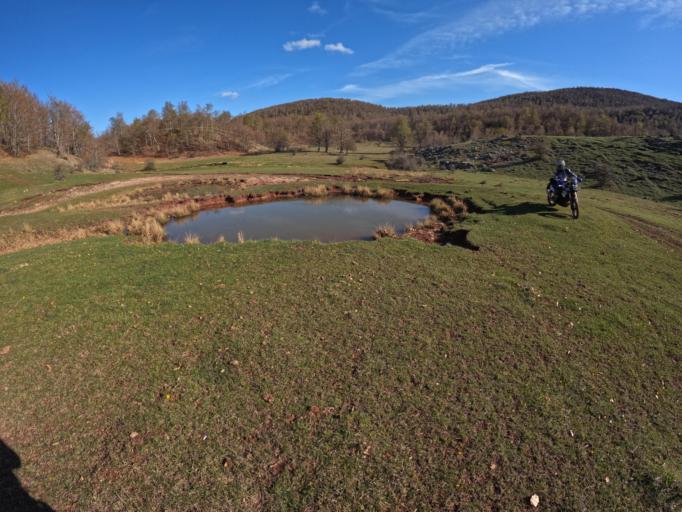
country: HR
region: Zadarska
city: Obrovac
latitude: 44.2828
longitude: 15.7059
